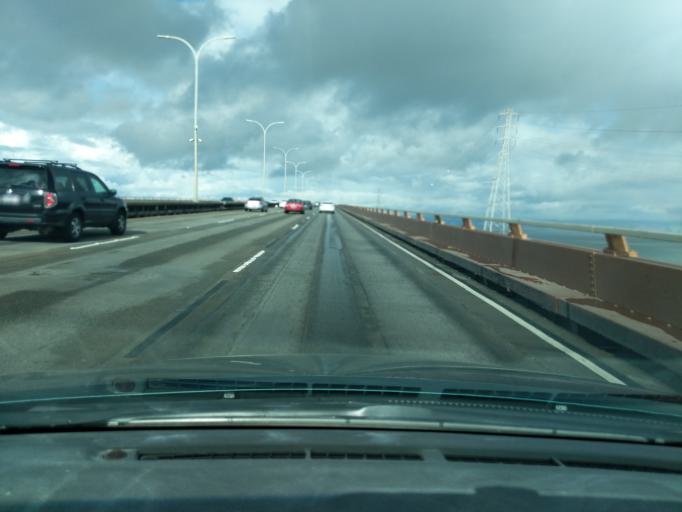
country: US
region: California
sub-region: San Mateo County
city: Foster City
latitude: 37.5809
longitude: -122.2541
